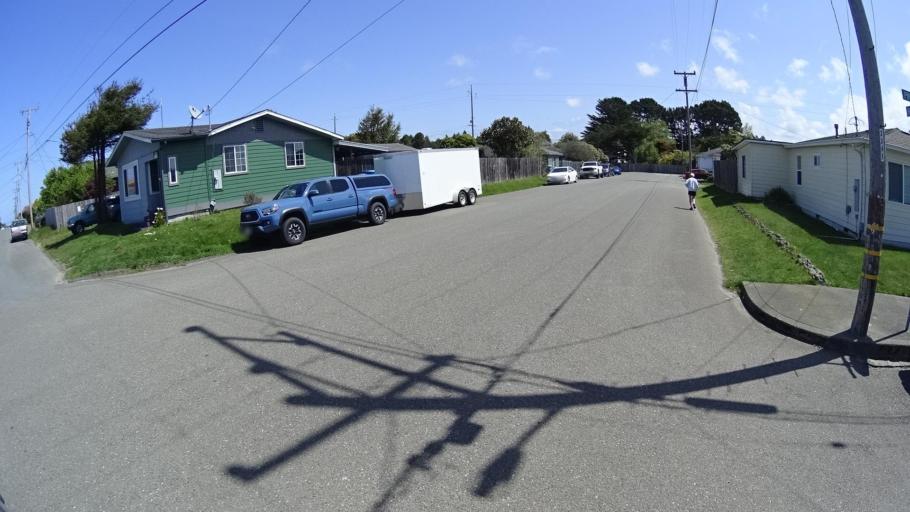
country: US
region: California
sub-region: Humboldt County
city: Bayview
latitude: 40.7766
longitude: -124.1727
